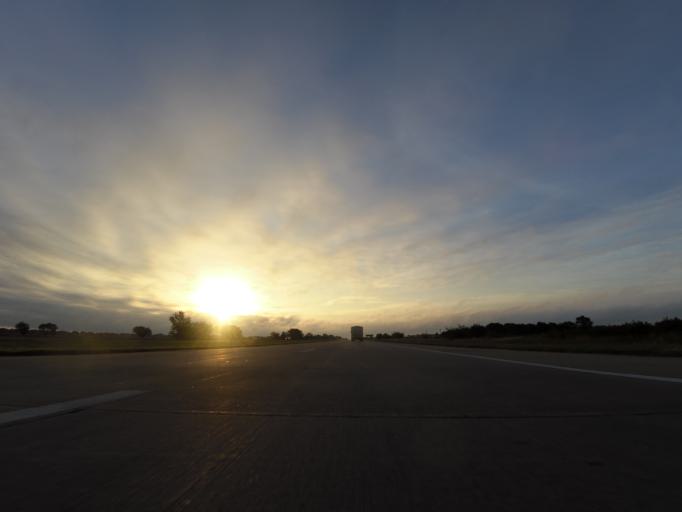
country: US
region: Kansas
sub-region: Reno County
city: Haven
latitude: 37.8924
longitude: -97.7605
